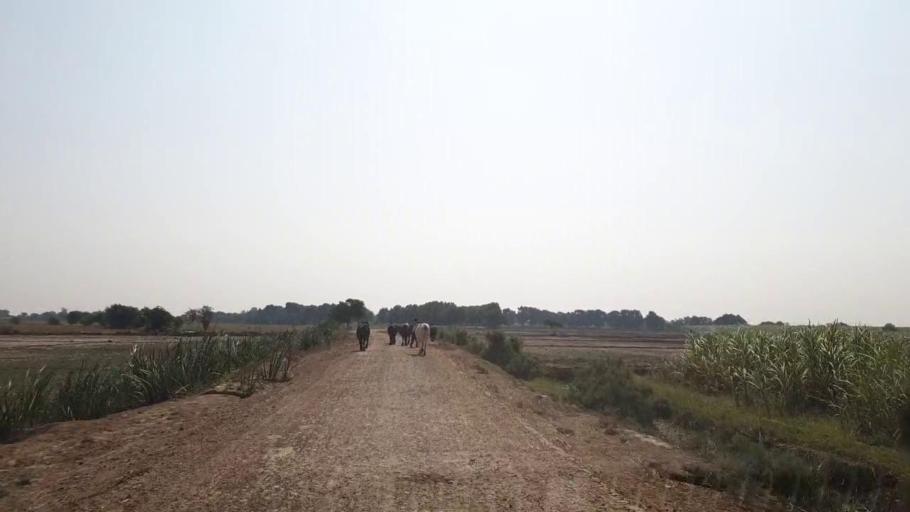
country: PK
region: Sindh
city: Tando Muhammad Khan
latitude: 25.0192
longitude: 68.4173
